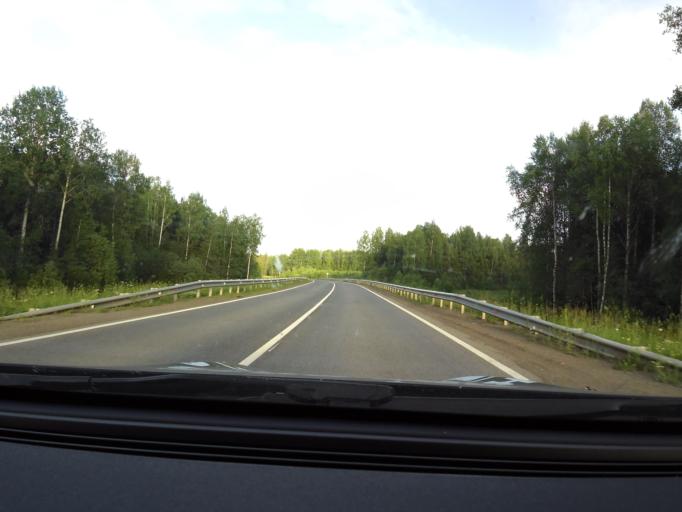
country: RU
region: Perm
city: Siva
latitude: 58.5413
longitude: 53.9218
